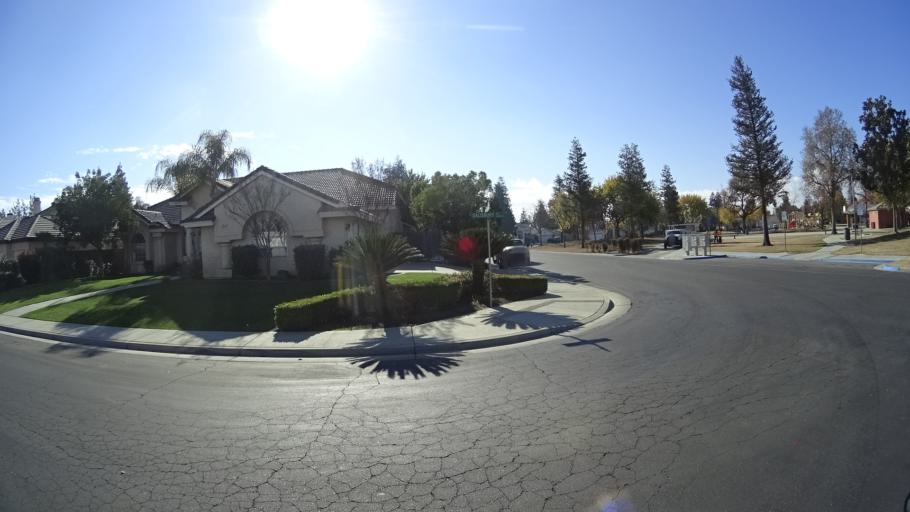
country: US
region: California
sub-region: Kern County
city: Greenacres
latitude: 35.3441
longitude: -119.1209
